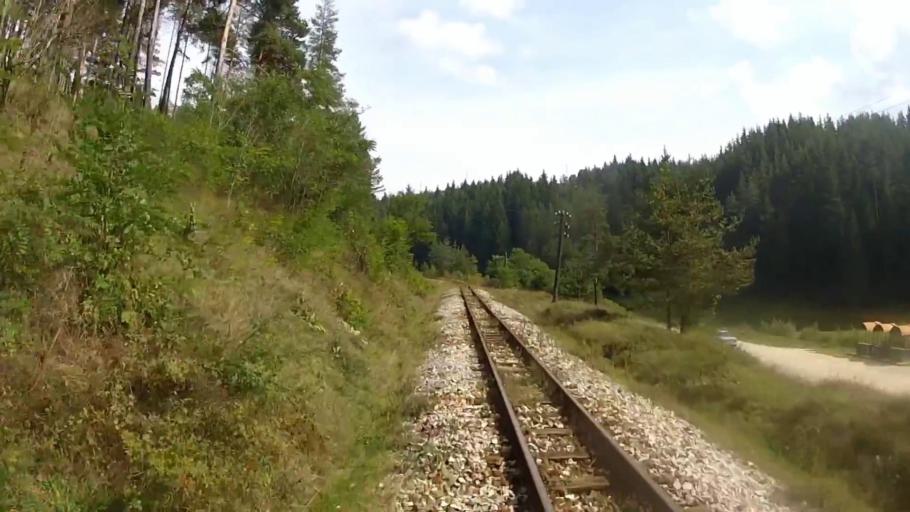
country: BG
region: Blagoevgrad
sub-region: Obshtina Yakoruda
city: Yakoruda
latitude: 42.0373
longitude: 23.8035
